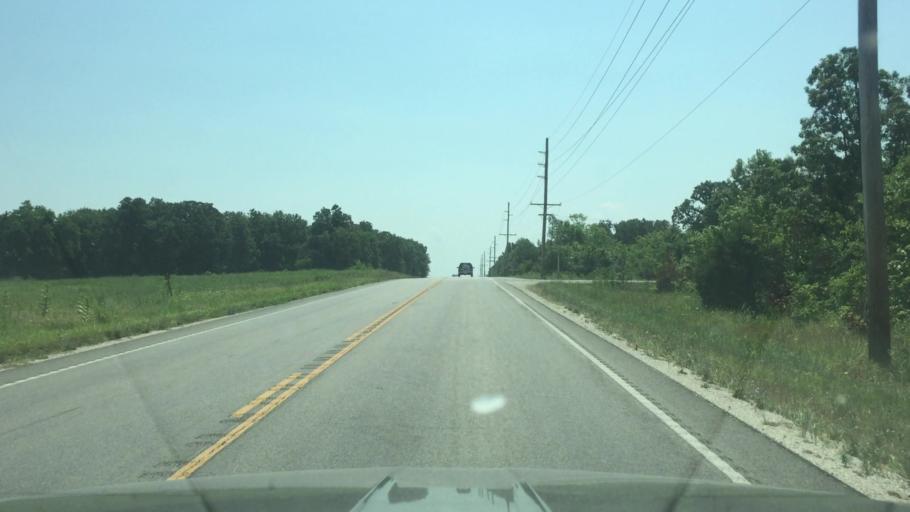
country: US
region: Missouri
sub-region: Miller County
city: Eldon
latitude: 38.3884
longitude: -92.6995
